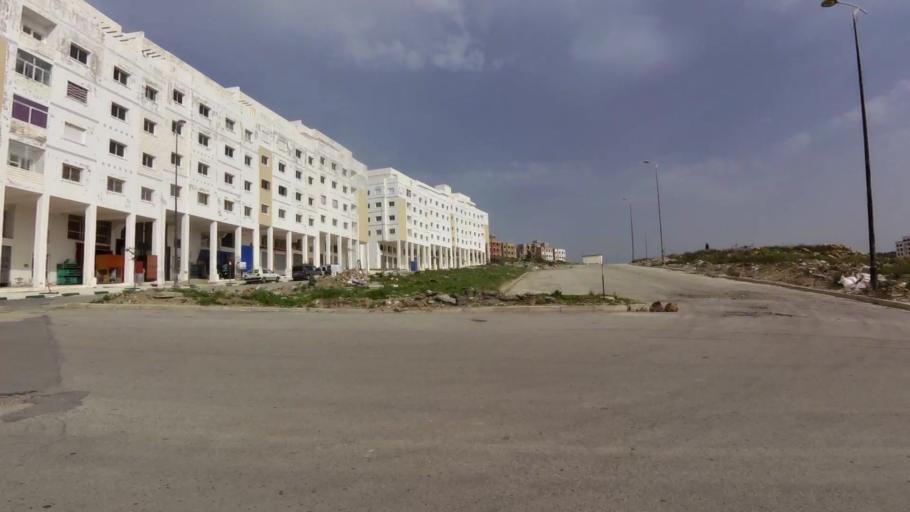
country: MA
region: Tanger-Tetouan
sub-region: Tanger-Assilah
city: Boukhalef
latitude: 35.7030
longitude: -5.9322
